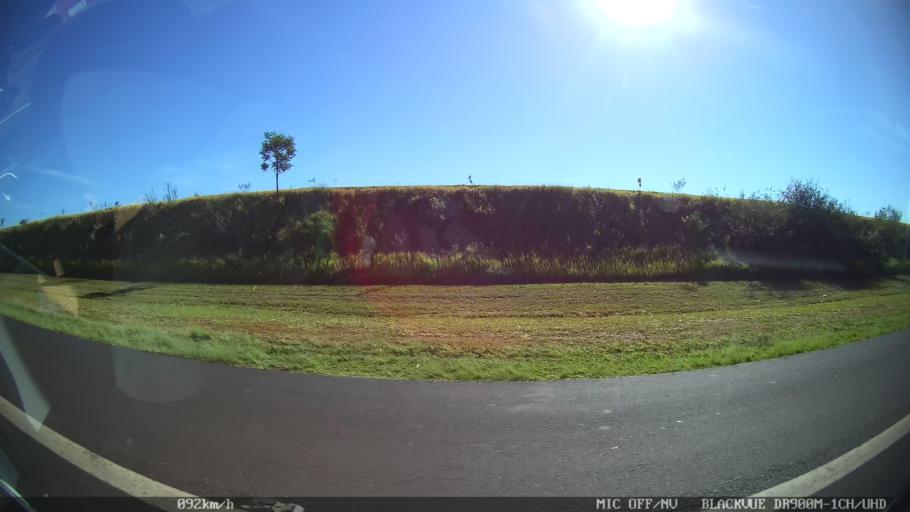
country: BR
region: Sao Paulo
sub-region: Franca
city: Franca
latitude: -20.5740
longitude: -47.3686
